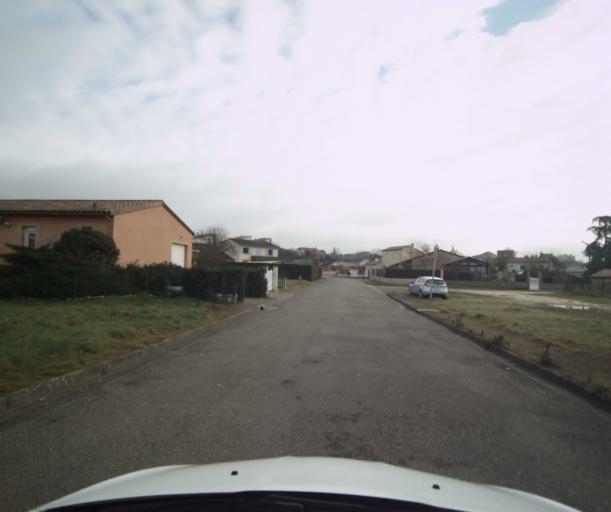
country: FR
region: Midi-Pyrenees
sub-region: Departement du Tarn-et-Garonne
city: Castelsarrasin
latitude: 44.0406
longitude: 1.0984
